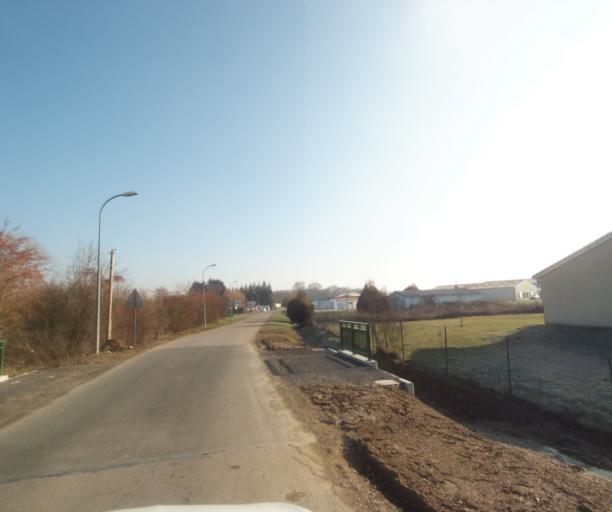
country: FR
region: Champagne-Ardenne
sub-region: Departement de la Haute-Marne
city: Wassy
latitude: 48.5008
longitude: 4.9353
